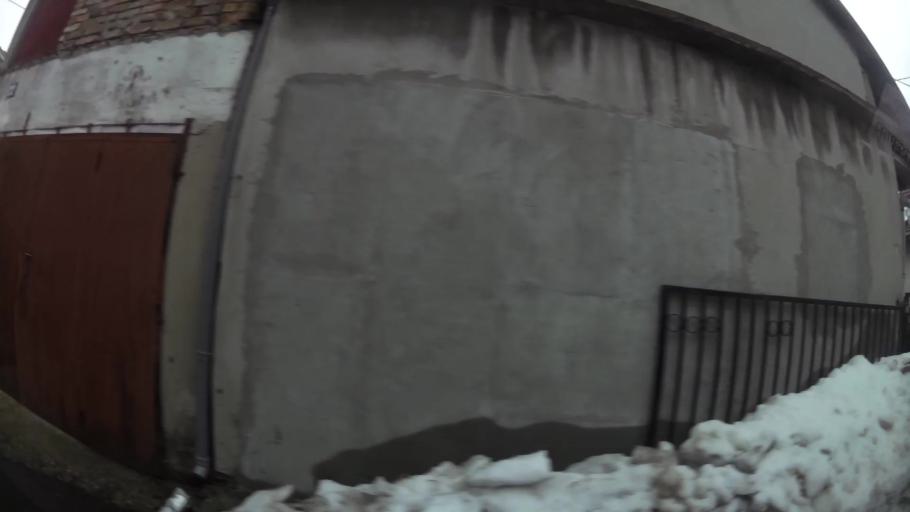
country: RS
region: Central Serbia
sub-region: Belgrade
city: Zvezdara
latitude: 44.7806
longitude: 20.5311
